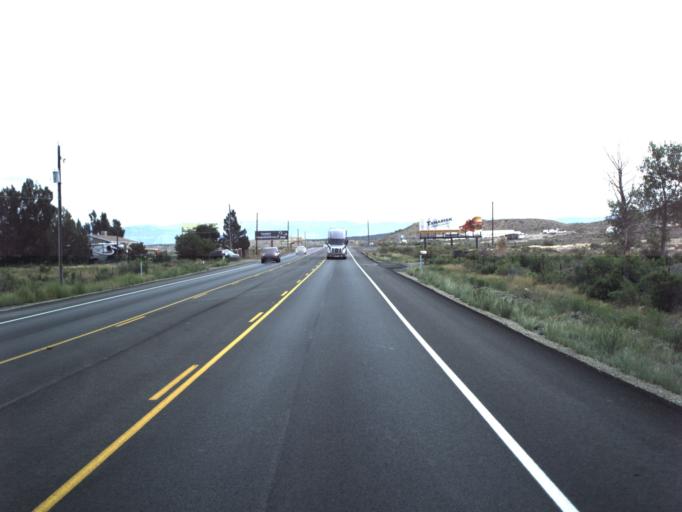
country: US
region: Utah
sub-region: Carbon County
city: Wellington
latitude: 39.5459
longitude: -110.6763
